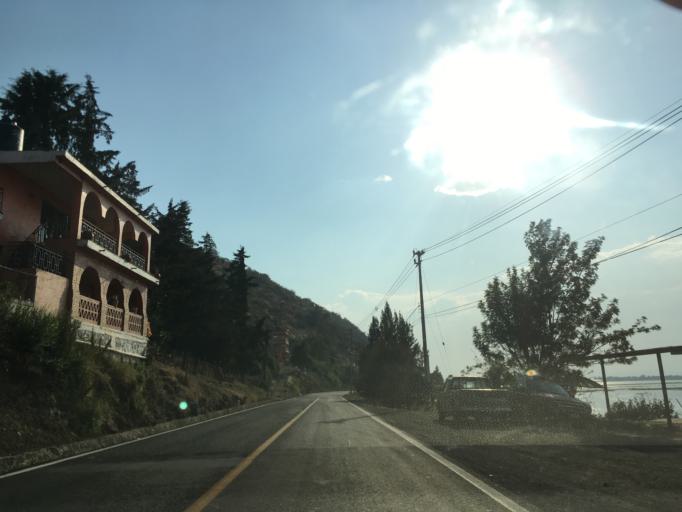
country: MX
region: Michoacan
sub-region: Zinapecuaro
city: Santa Clara del Tule
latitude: 19.8092
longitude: -100.8509
